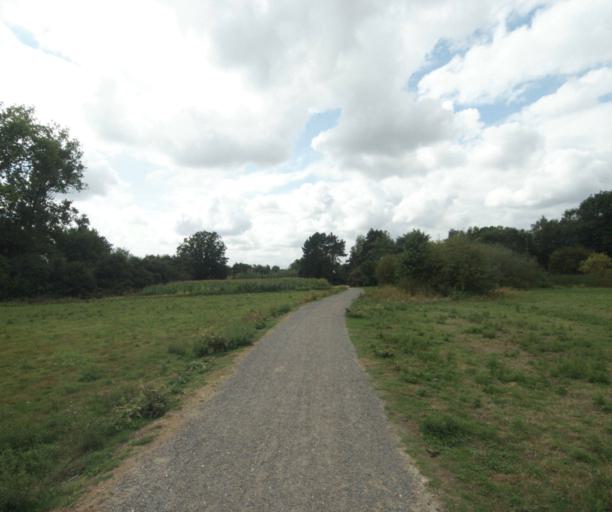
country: FR
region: Nord-Pas-de-Calais
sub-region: Departement du Nord
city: Villeneuve-d'Ascq
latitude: 50.6296
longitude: 3.1722
